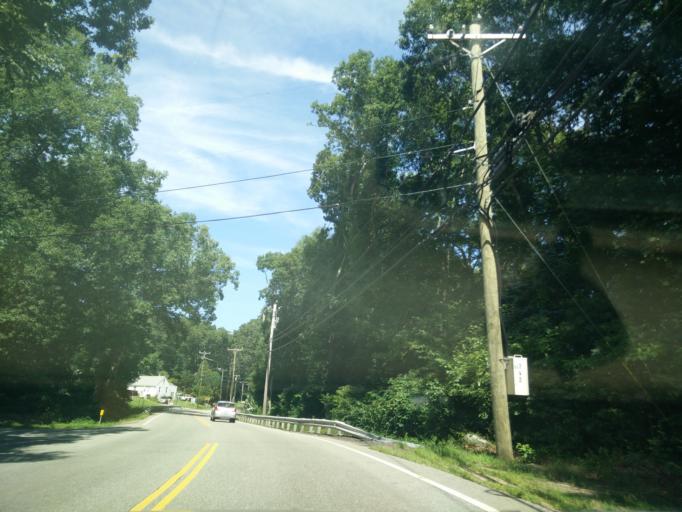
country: US
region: Connecticut
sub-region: Middlesex County
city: Clinton
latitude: 41.3050
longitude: -72.5343
